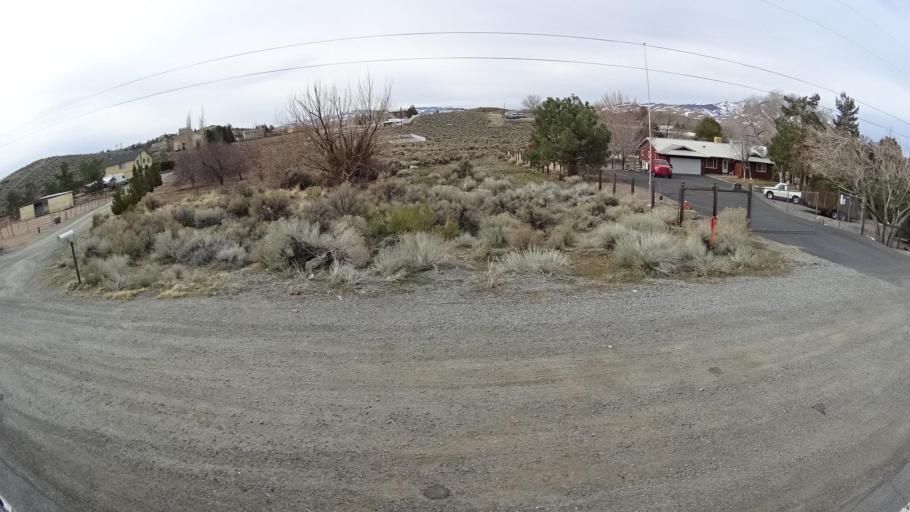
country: US
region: Nevada
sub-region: Washoe County
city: Golden Valley
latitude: 39.6069
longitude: -119.8120
